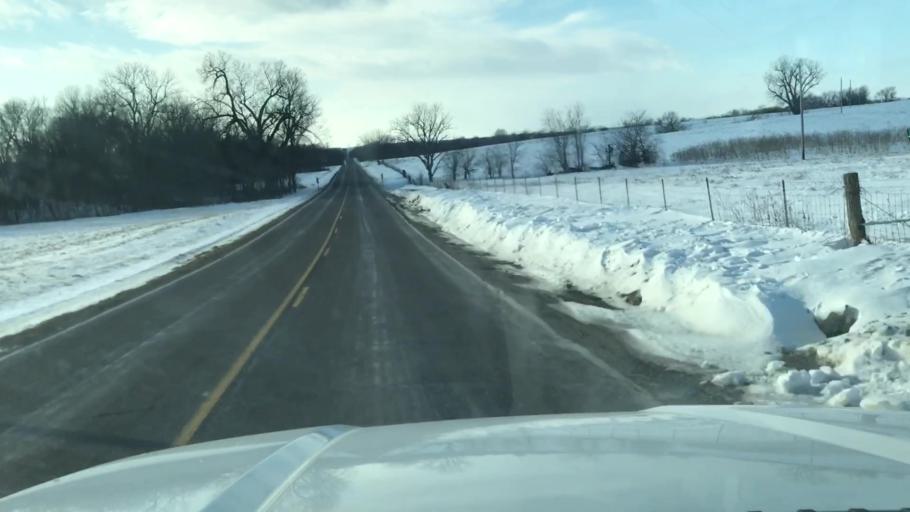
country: US
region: Missouri
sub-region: Nodaway County
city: Maryville
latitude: 40.2018
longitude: -94.9346
